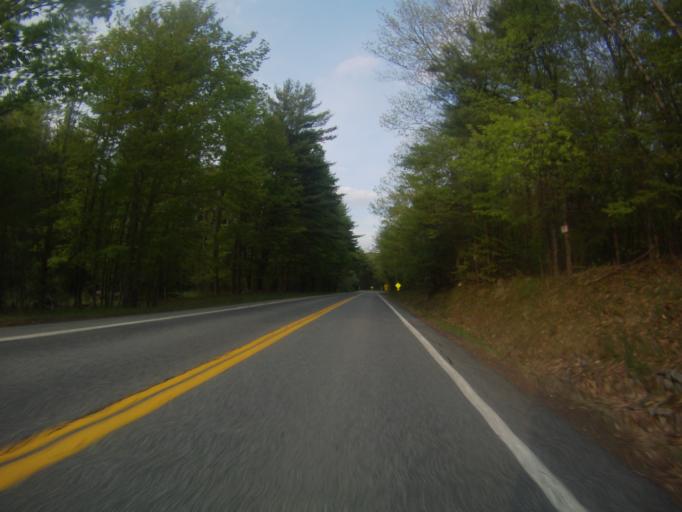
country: US
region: New York
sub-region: Essex County
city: Ticonderoga
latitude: 43.7579
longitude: -73.5259
